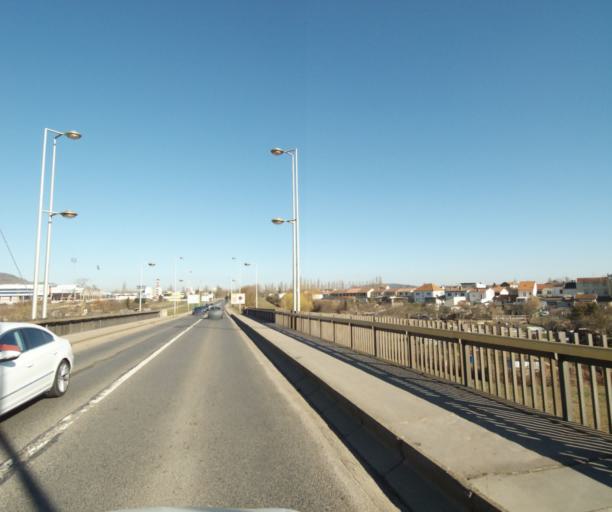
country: FR
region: Lorraine
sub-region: Departement de Meurthe-et-Moselle
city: Tomblaine
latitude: 48.6914
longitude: 6.2065
